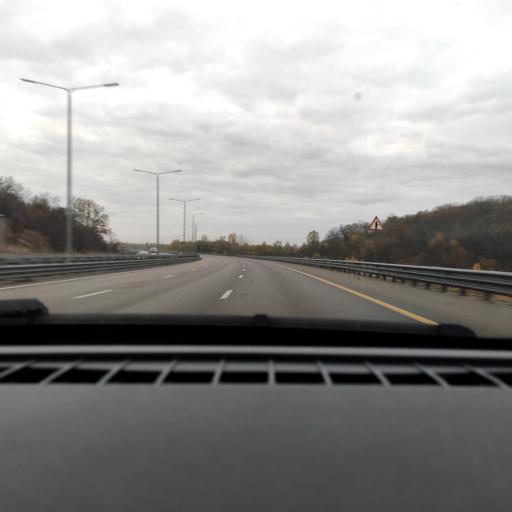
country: RU
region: Voronezj
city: Podgornoye
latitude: 51.7995
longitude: 39.2557
